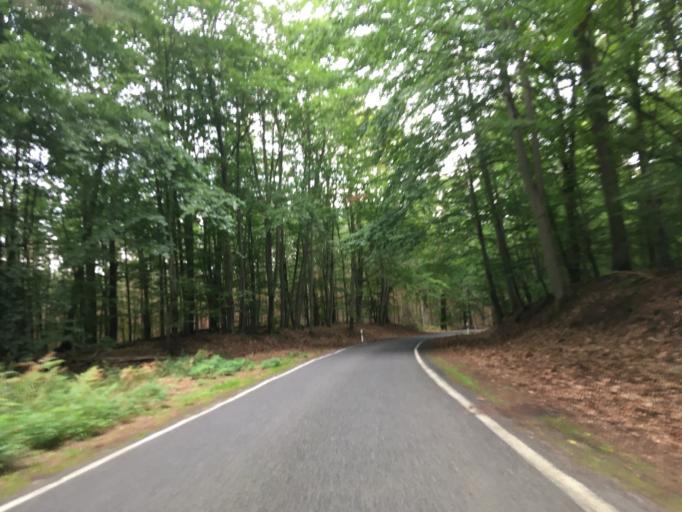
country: DE
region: Brandenburg
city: Althuttendorf
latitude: 53.0521
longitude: 13.8470
